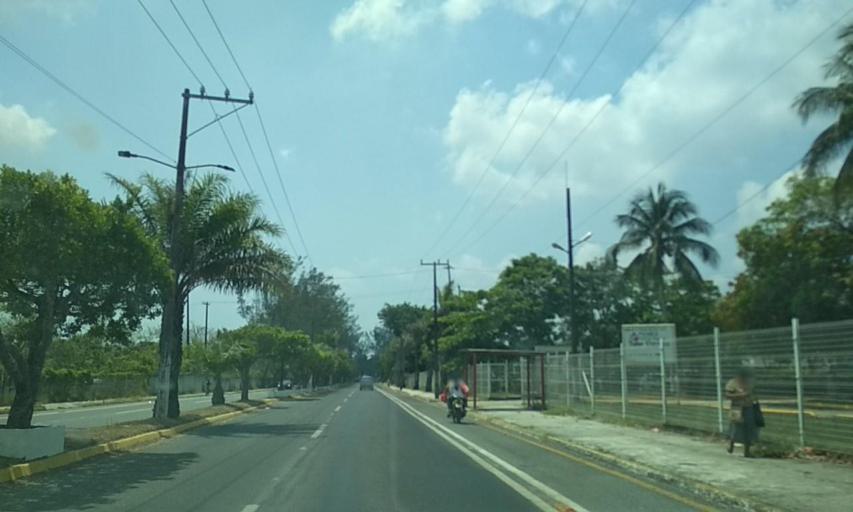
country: MX
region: Veracruz
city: Las Choapas
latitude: 17.9288
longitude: -94.0960
